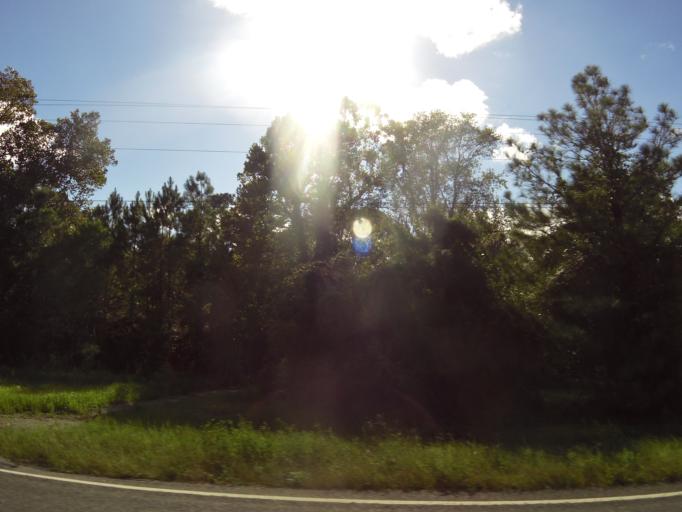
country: US
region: Georgia
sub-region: Camden County
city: Kingsland
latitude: 30.8753
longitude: -81.7053
